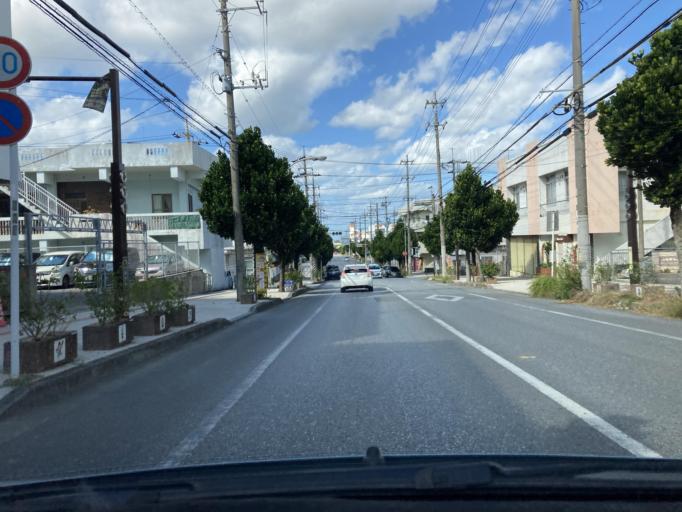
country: JP
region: Okinawa
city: Okinawa
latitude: 26.3327
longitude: 127.7923
